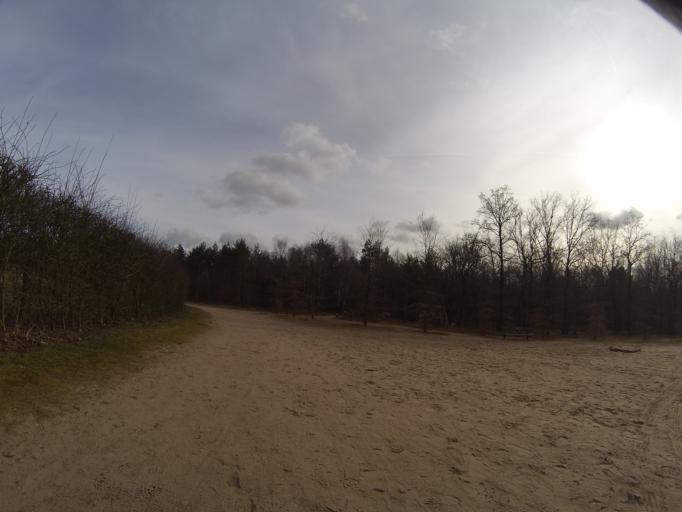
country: NL
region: Utrecht
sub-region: Gemeente Utrechtse Heuvelrug
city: Maarn
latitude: 52.0901
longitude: 5.3417
